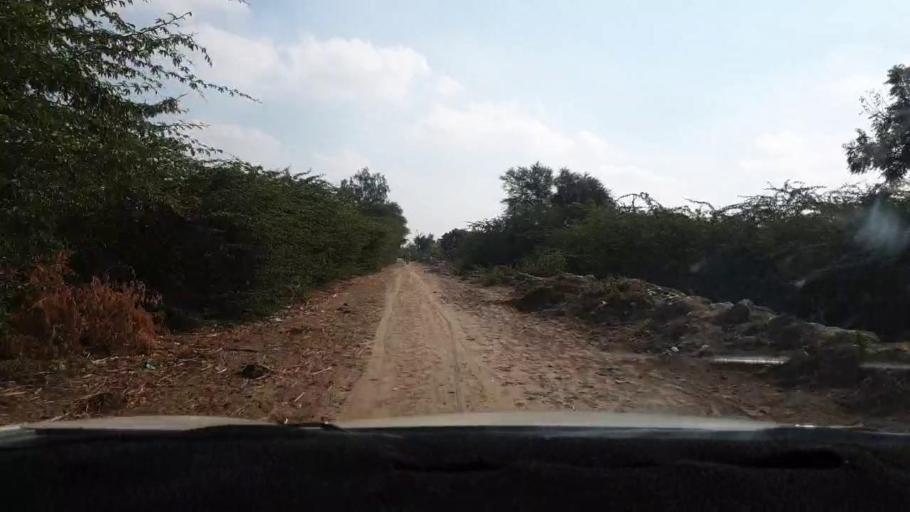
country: PK
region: Sindh
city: Berani
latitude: 25.7593
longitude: 68.9931
